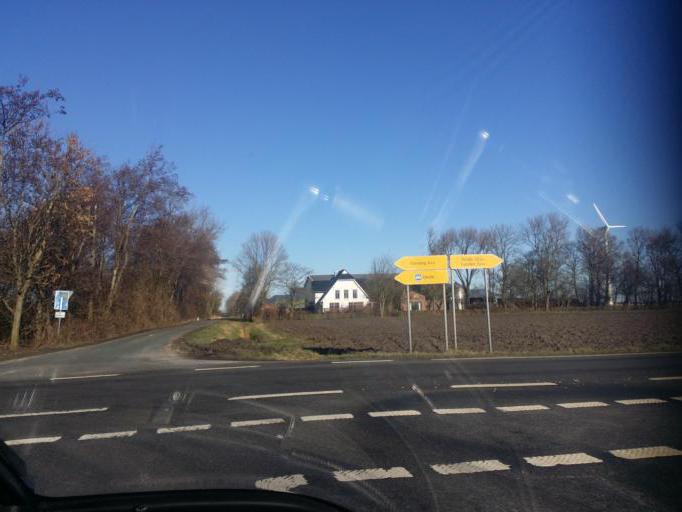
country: DE
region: Schleswig-Holstein
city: Groven
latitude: 54.3100
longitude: 8.9729
